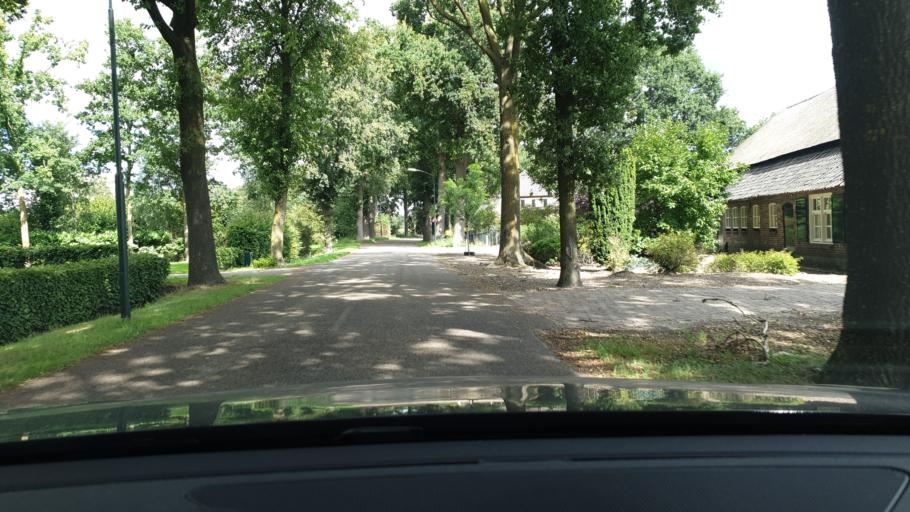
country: NL
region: North Brabant
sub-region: Gemeente Veghel
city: Zijtaart
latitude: 51.5986
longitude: 5.5395
